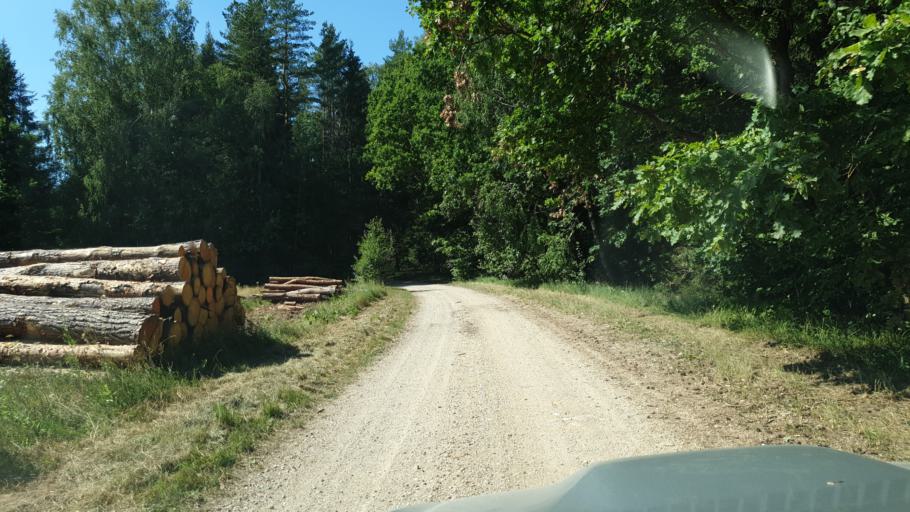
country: LT
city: Sirvintos
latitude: 54.9008
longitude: 24.8924
